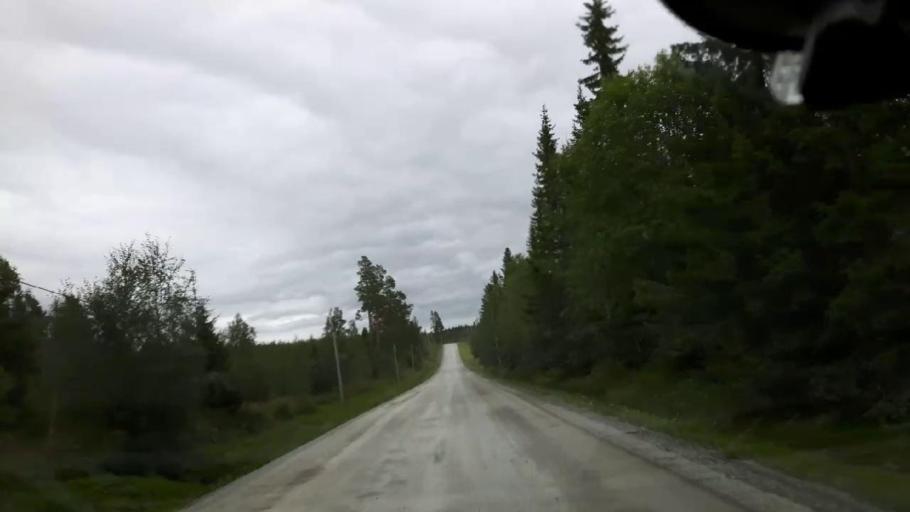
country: SE
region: Jaemtland
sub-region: OEstersunds Kommun
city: Brunflo
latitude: 63.0966
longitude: 15.1282
